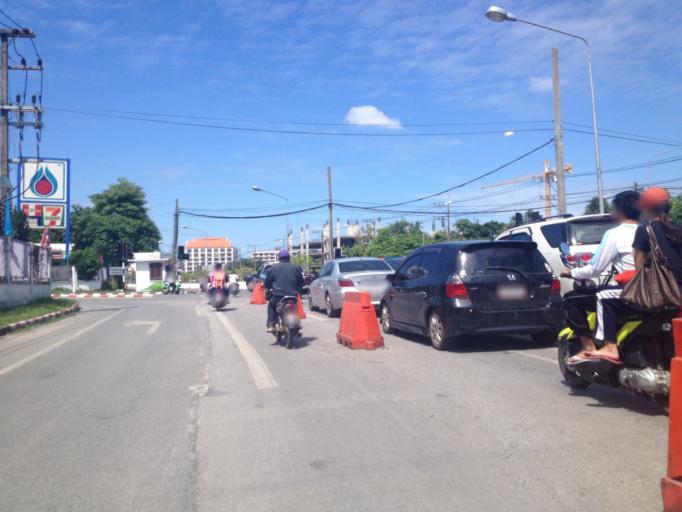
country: TH
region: Chiang Mai
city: Chiang Mai
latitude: 18.7950
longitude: 98.9619
